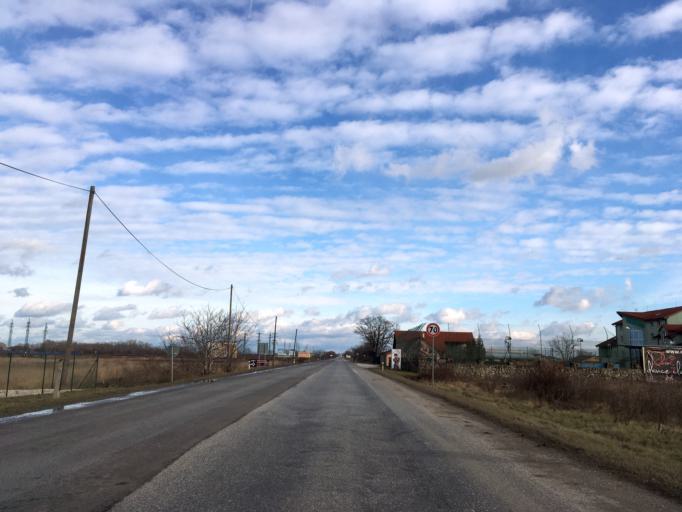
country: SK
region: Bratislavsky
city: Senec
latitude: 48.2050
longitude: 17.4147
